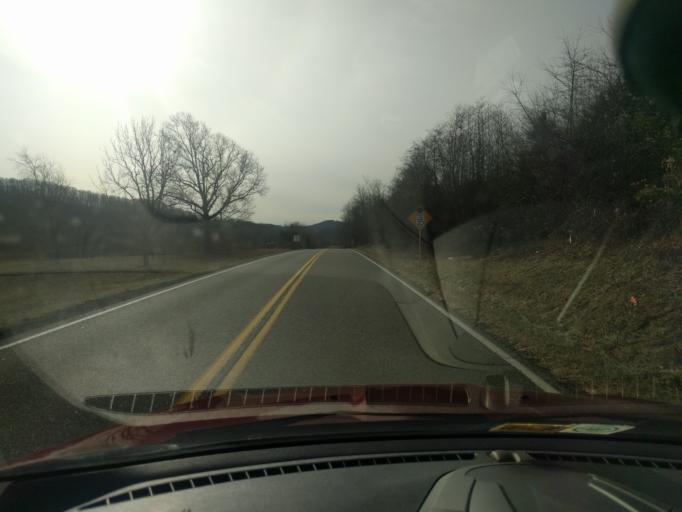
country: US
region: Virginia
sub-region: Augusta County
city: Stuarts Draft
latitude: 38.0251
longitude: -79.1352
